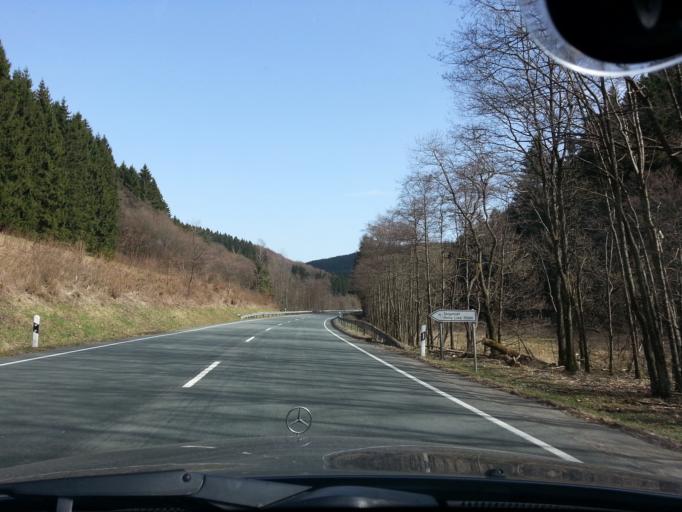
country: DE
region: North Rhine-Westphalia
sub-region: Regierungsbezirk Arnsberg
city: Bad Fredeburg
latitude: 51.2316
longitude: 8.3530
